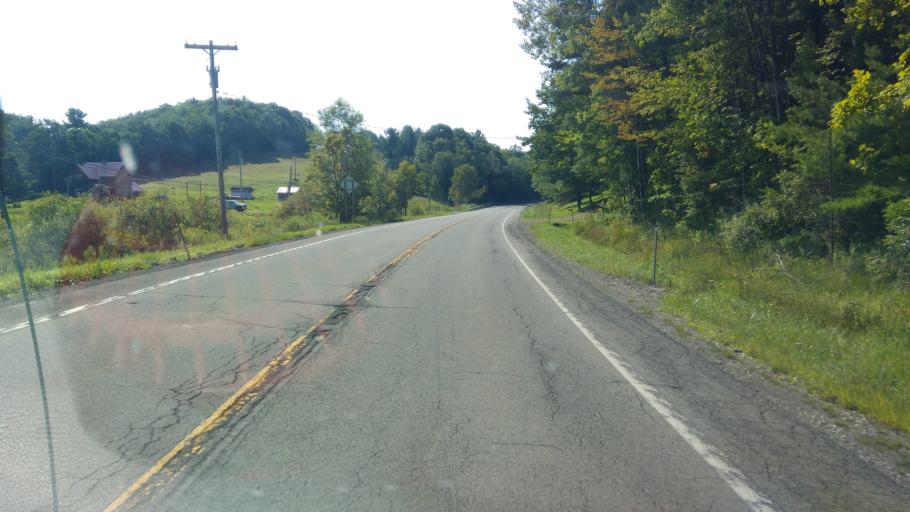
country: US
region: New York
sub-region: Allegany County
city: Cuba
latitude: 42.1825
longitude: -78.2572
